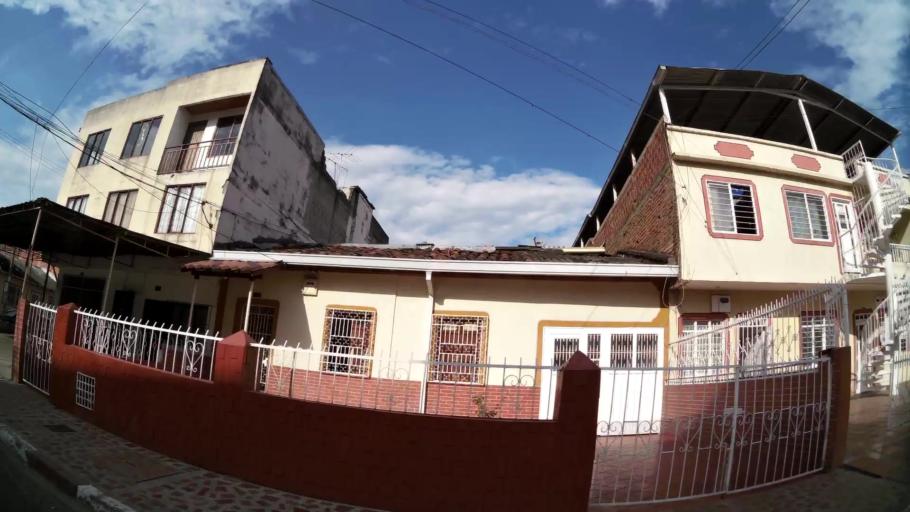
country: CO
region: Valle del Cauca
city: Cali
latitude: 3.4696
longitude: -76.5127
